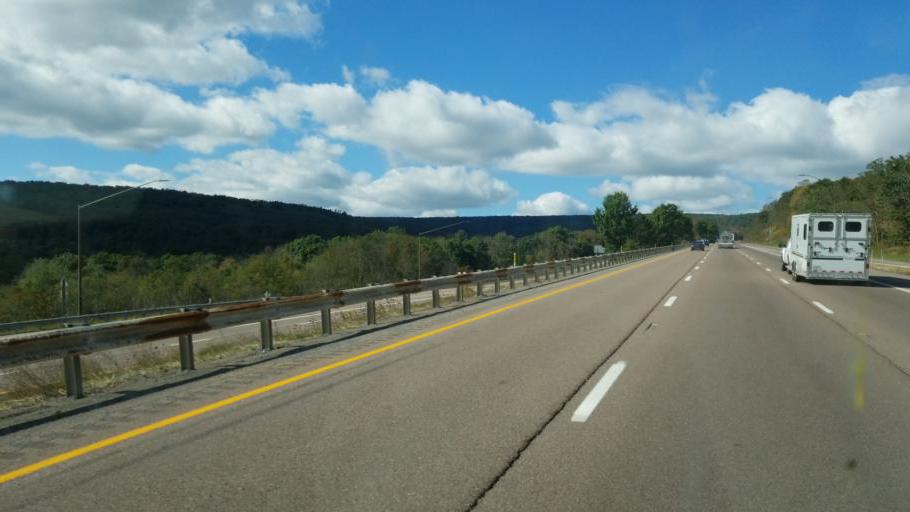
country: US
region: Maryland
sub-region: Allegany County
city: Frostburg
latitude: 39.6402
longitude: -78.9494
